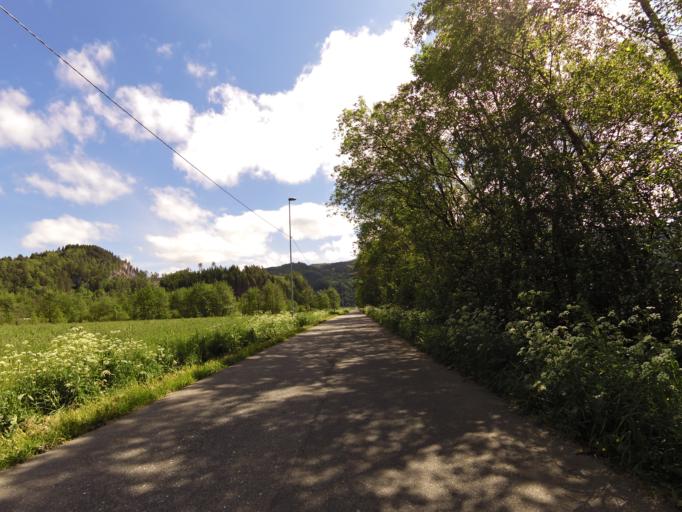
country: NO
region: Vest-Agder
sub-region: Kvinesdal
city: Liknes
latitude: 58.3062
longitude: 6.9384
